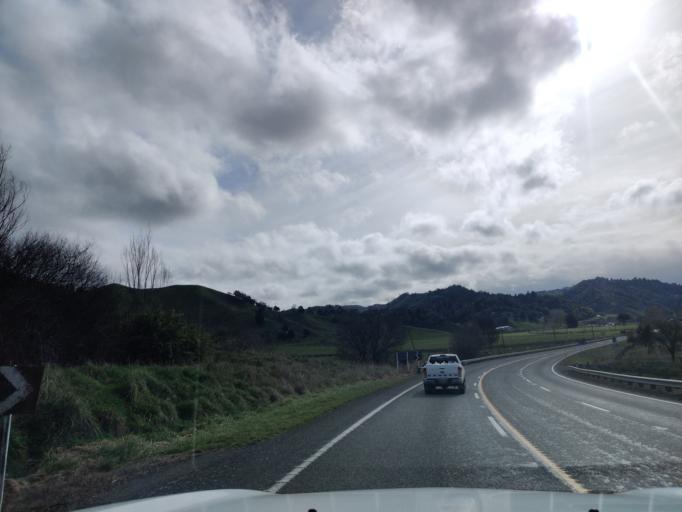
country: NZ
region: Manawatu-Wanganui
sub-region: Ruapehu District
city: Waiouru
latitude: -39.8229
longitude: 175.7762
